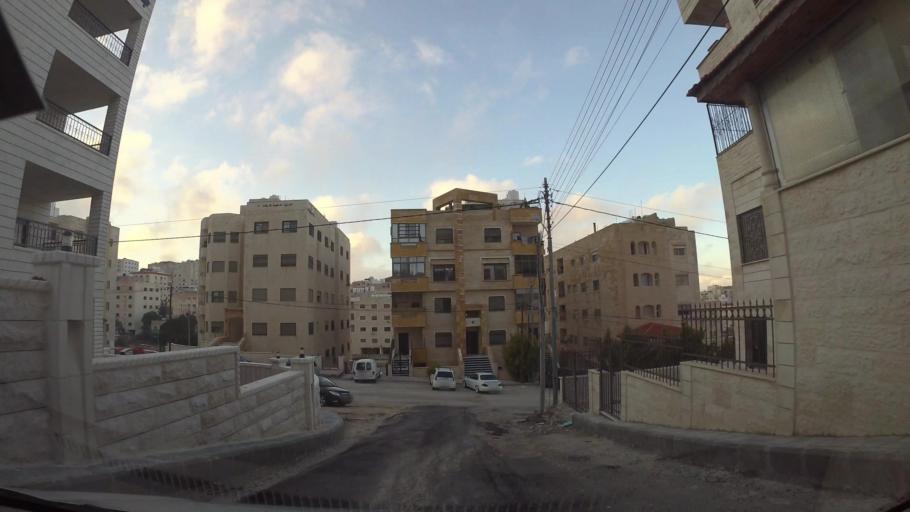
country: JO
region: Amman
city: Al Jubayhah
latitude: 32.0513
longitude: 35.8983
